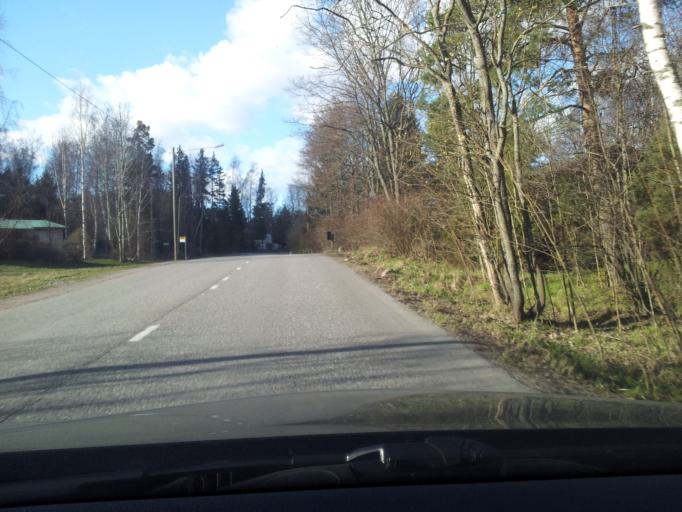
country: FI
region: Uusimaa
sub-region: Helsinki
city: Espoo
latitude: 60.1372
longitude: 24.6824
